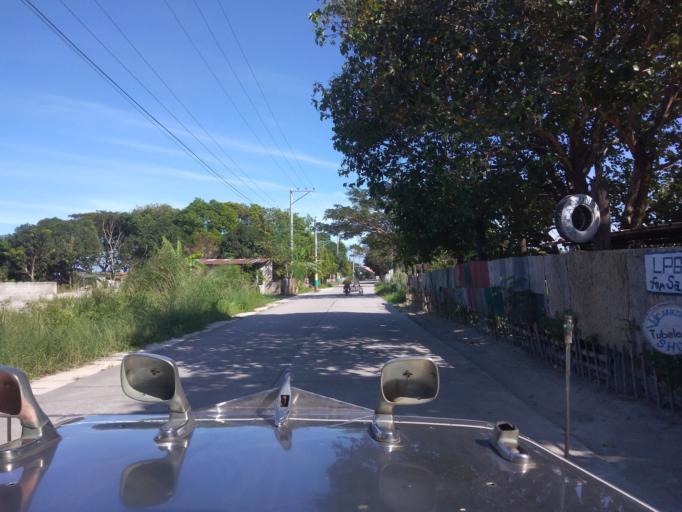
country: PH
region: Central Luzon
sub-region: Province of Pampanga
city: Magliman
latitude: 15.0281
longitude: 120.6344
